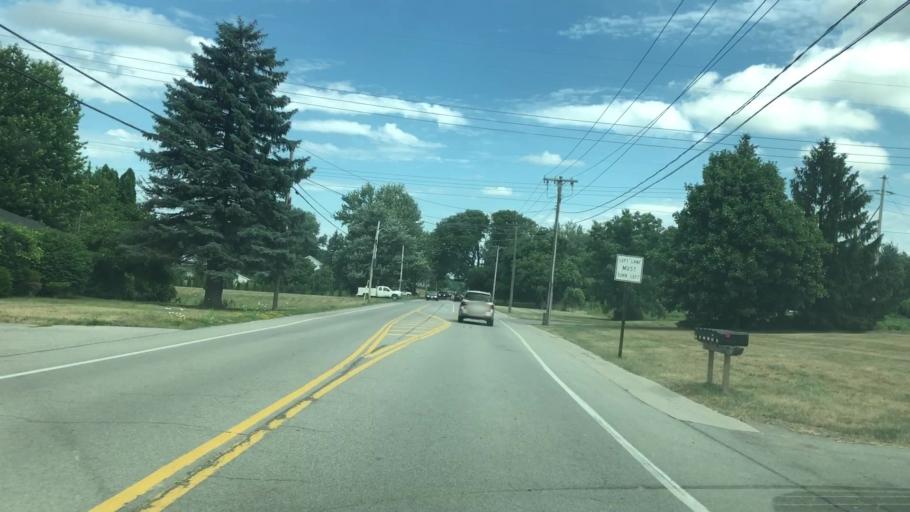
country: US
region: New York
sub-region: Wayne County
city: Macedon
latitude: 43.0695
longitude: -77.3611
